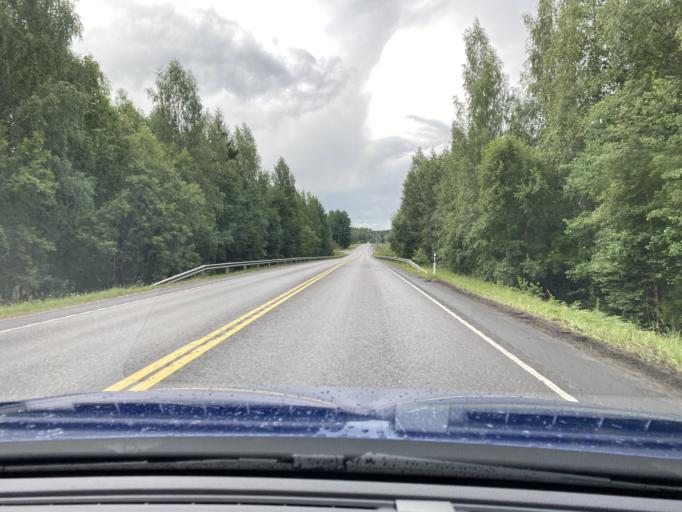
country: FI
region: Uusimaa
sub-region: Helsinki
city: Hyvinge
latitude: 60.5714
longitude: 24.8031
